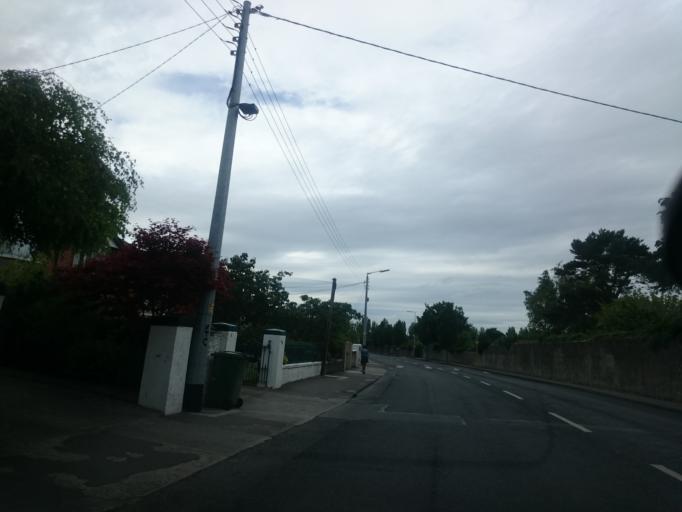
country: IE
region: Leinster
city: Templeogue
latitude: 53.3048
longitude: -6.2996
